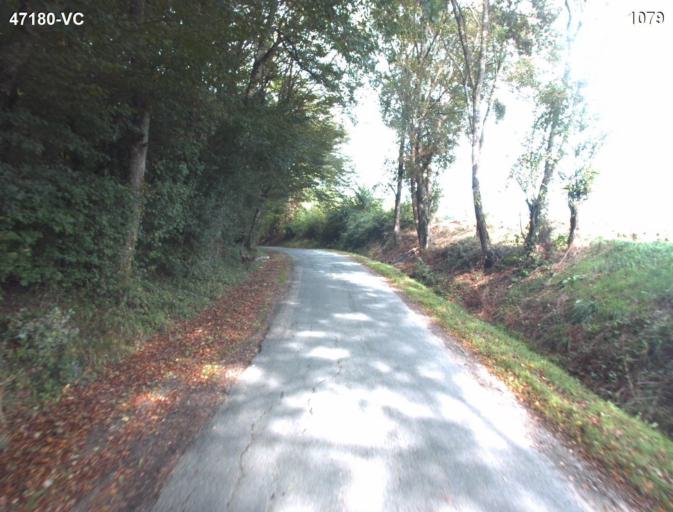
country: FR
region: Aquitaine
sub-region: Departement du Lot-et-Garonne
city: Sainte-Colombe-en-Bruilhois
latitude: 44.1808
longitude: 0.4405
